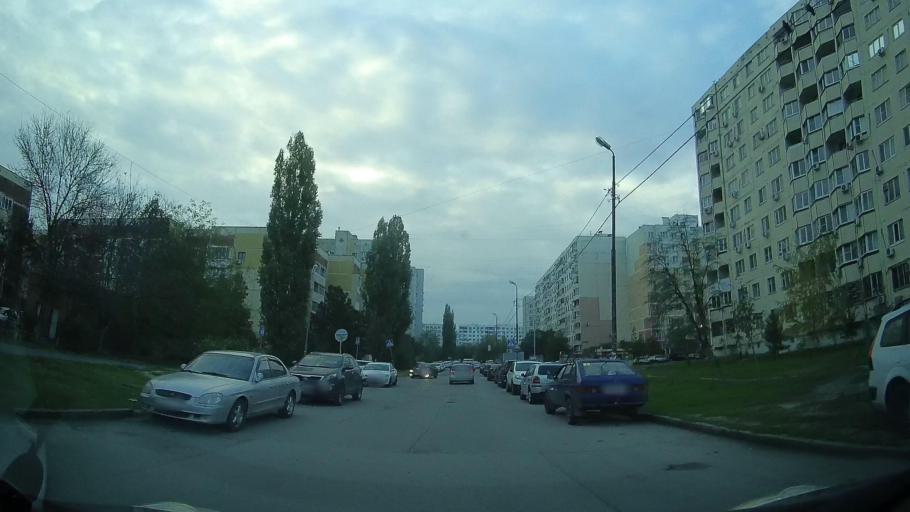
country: RU
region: Rostov
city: Severnyy
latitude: 47.2601
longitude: 39.6431
